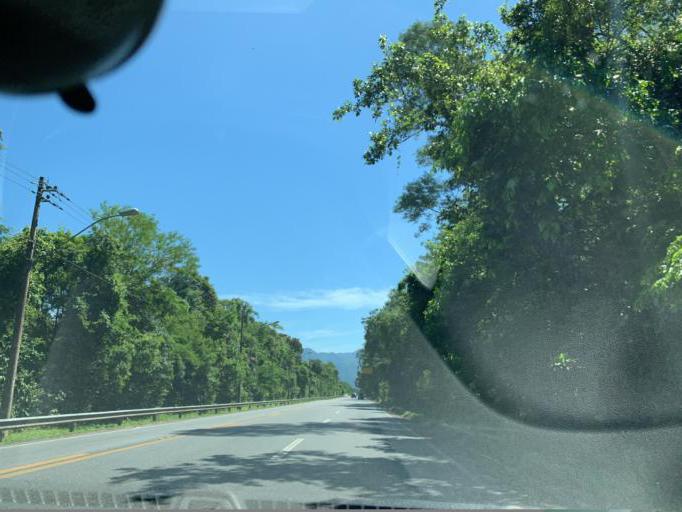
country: BR
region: Sao Paulo
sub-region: Bertioga
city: Bertioga
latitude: -23.7734
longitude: -46.0464
